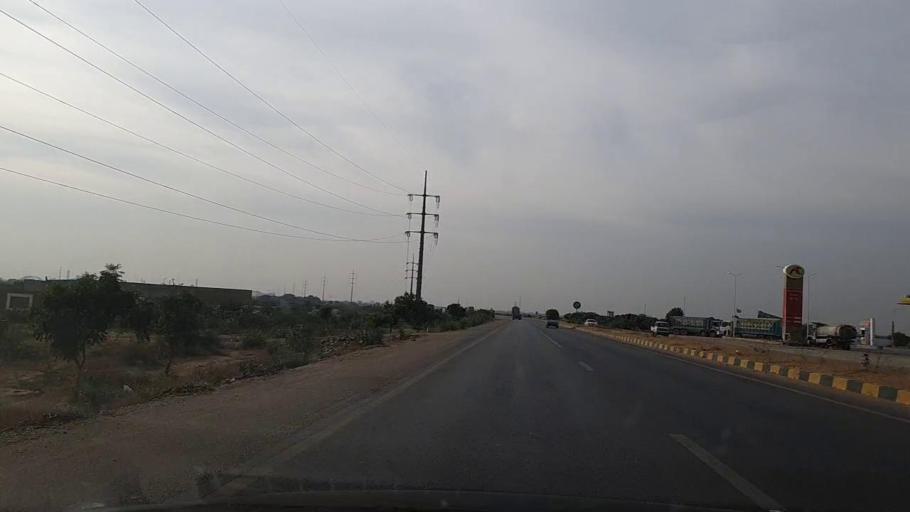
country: PK
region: Sindh
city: Gharo
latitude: 24.8357
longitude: 67.4547
